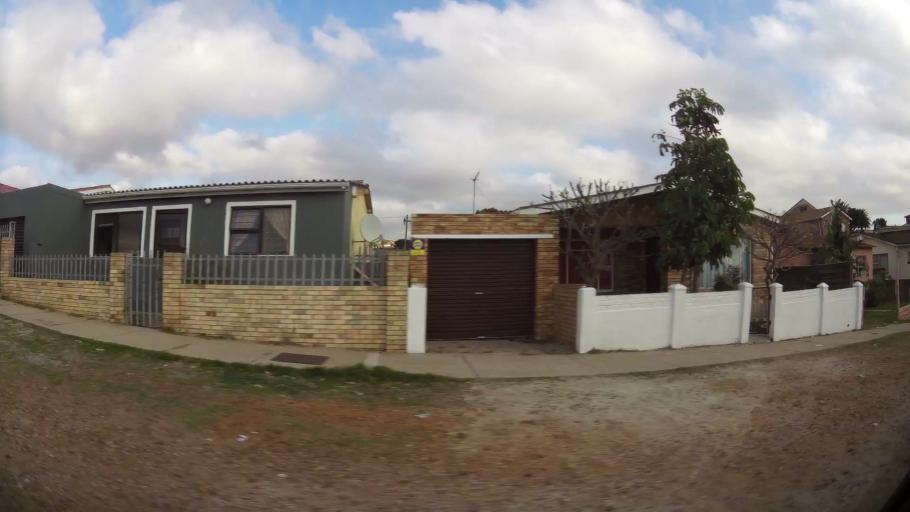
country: ZA
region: Eastern Cape
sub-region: Nelson Mandela Bay Metropolitan Municipality
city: Port Elizabeth
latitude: -33.9139
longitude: 25.5499
